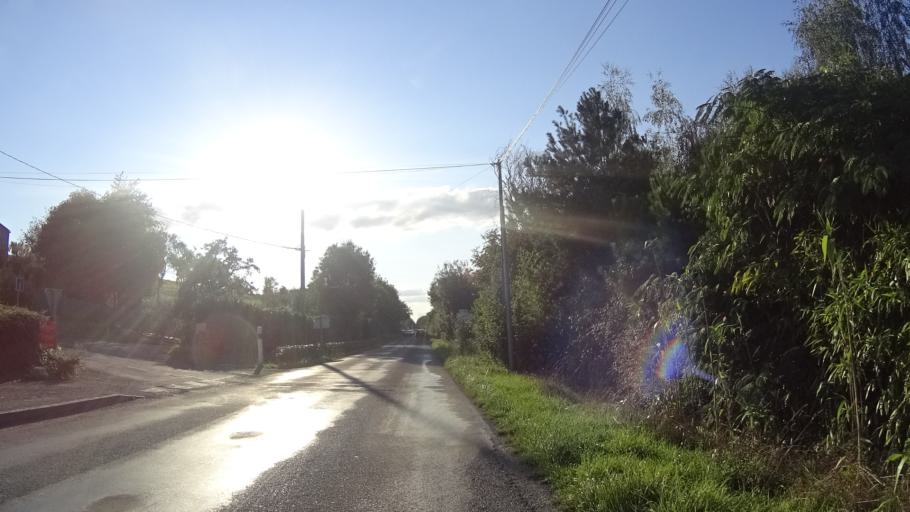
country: FR
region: Pays de la Loire
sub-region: Departement de Maine-et-Loire
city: Lire
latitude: 47.3452
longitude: -1.1702
